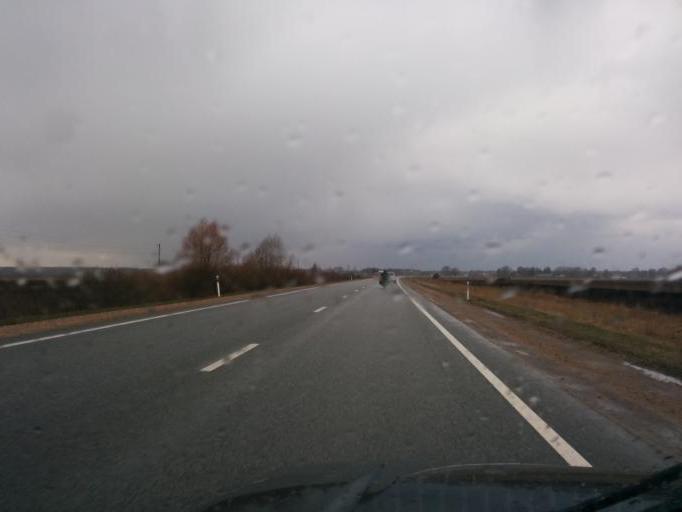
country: LV
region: Marupe
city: Marupe
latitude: 56.8635
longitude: 23.9792
